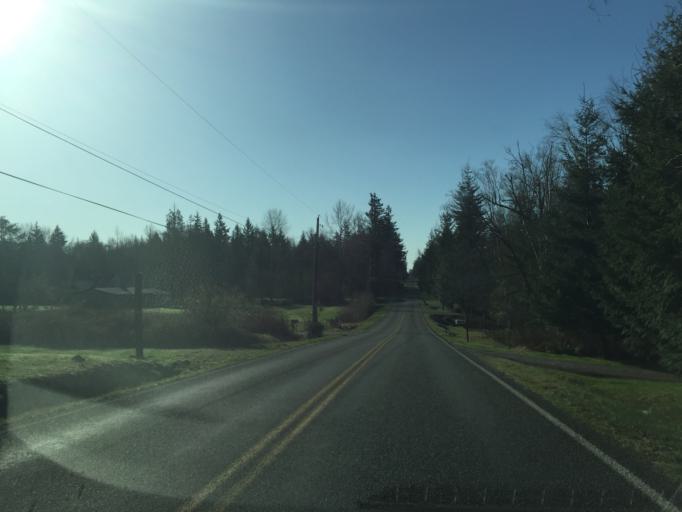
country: US
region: Washington
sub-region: Whatcom County
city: Marietta-Alderwood
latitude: 48.8129
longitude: -122.5080
